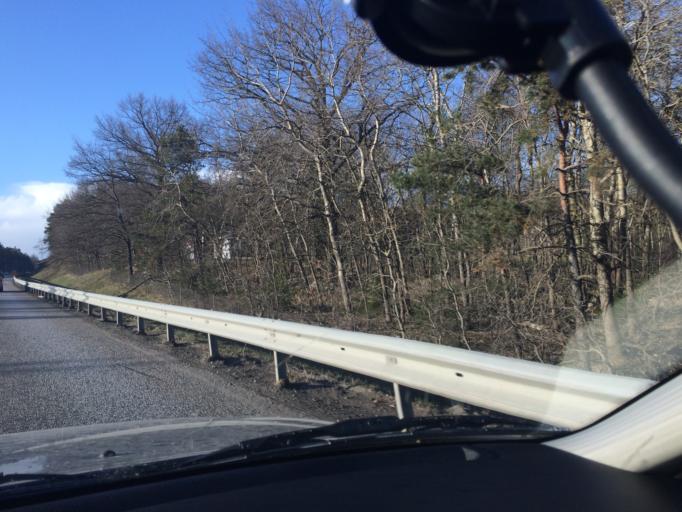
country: SE
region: Stockholm
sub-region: Jarfalla Kommun
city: Jakobsberg
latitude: 59.4330
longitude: 17.8463
